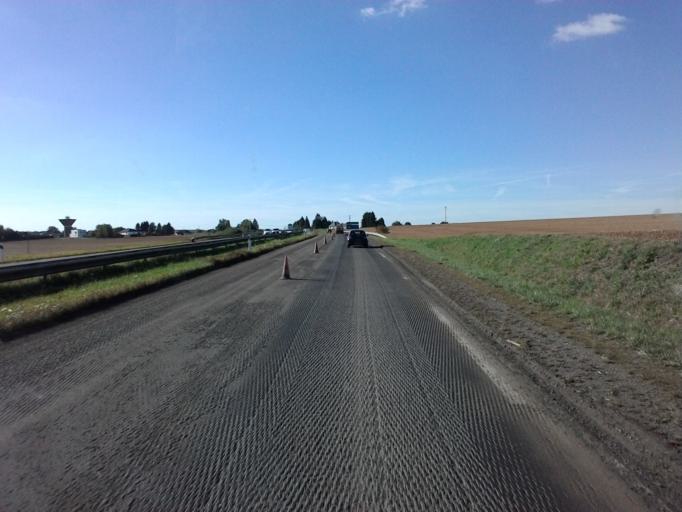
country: FR
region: Lorraine
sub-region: Departement de Meurthe-et-Moselle
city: Haucourt-Moulaine
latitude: 49.4998
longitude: 5.8011
